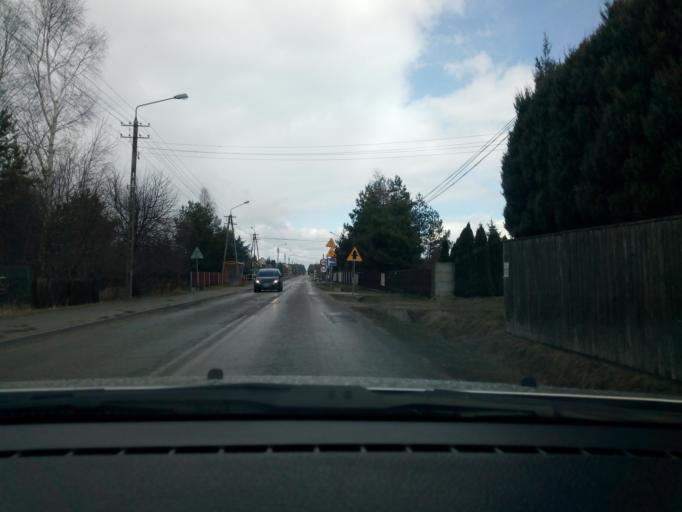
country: PL
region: Swietokrzyskie
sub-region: Powiat skarzyski
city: Skarzysko Koscielne
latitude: 51.1554
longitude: 20.9093
